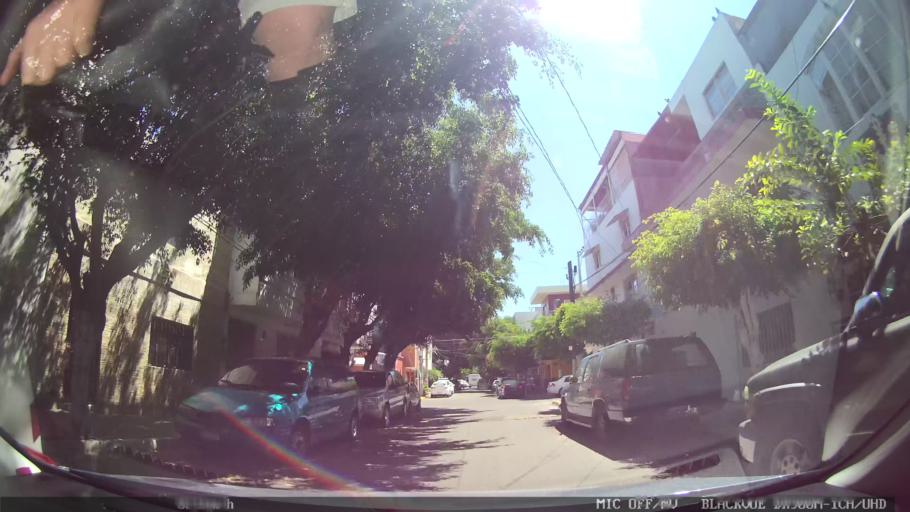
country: MX
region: Jalisco
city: Tlaquepaque
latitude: 20.6712
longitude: -103.2825
